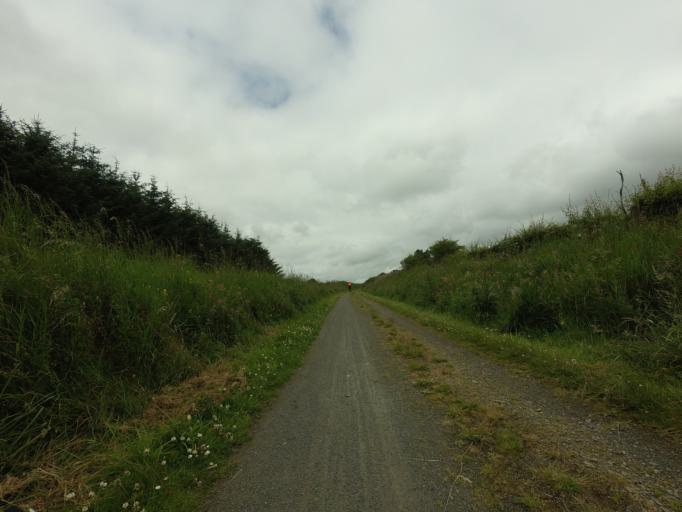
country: GB
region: Scotland
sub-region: Aberdeenshire
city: Mintlaw
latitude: 57.4981
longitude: -2.1407
